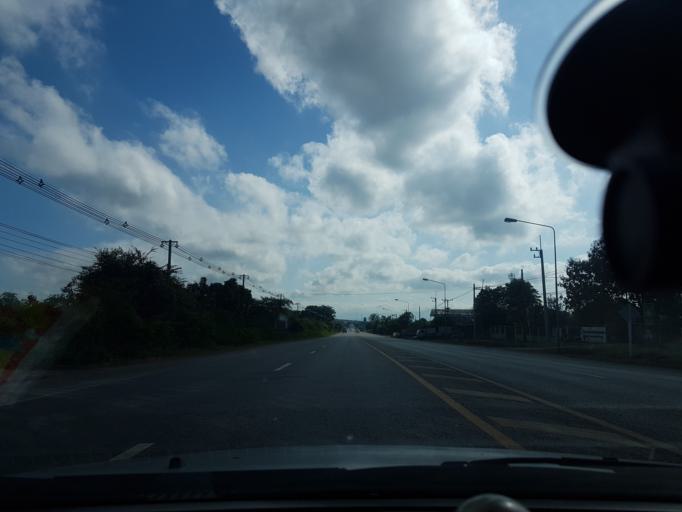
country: TH
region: Lop Buri
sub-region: Amphoe Tha Luang
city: Tha Luang
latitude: 15.0791
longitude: 101.0226
